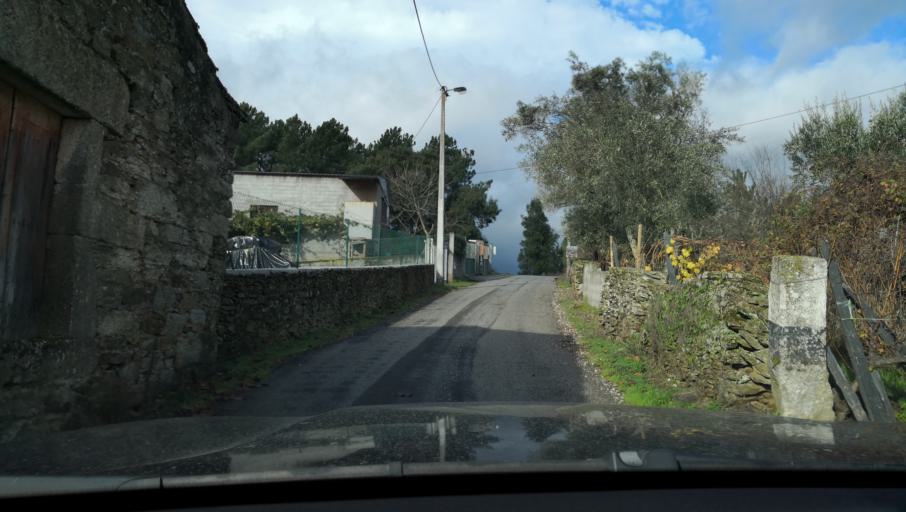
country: PT
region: Vila Real
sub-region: Vila Real
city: Vila Real
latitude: 41.2687
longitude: -7.7153
